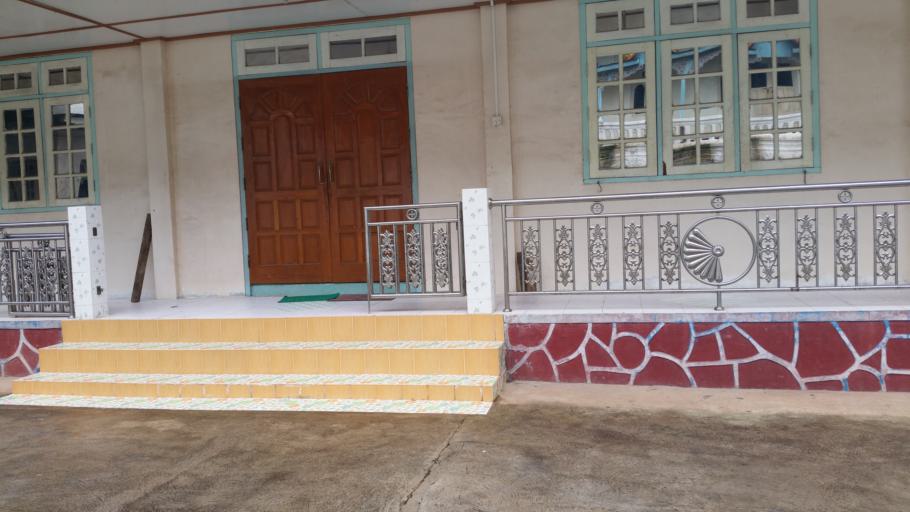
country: MM
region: Shan
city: Taunggyi
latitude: 20.5780
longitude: 96.9623
